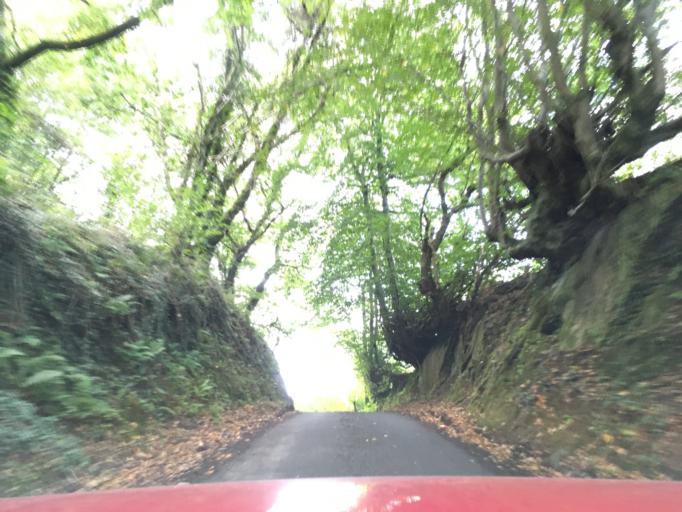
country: GB
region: Wales
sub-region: Cardiff
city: Pentyrch
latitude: 51.5584
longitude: -3.2759
